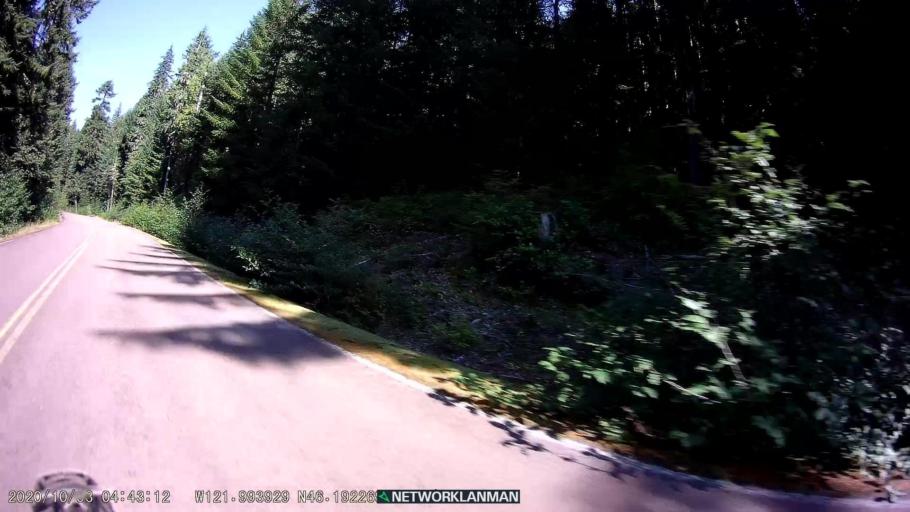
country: US
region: Washington
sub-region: Lewis County
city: Morton
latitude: 46.1925
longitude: -121.9938
